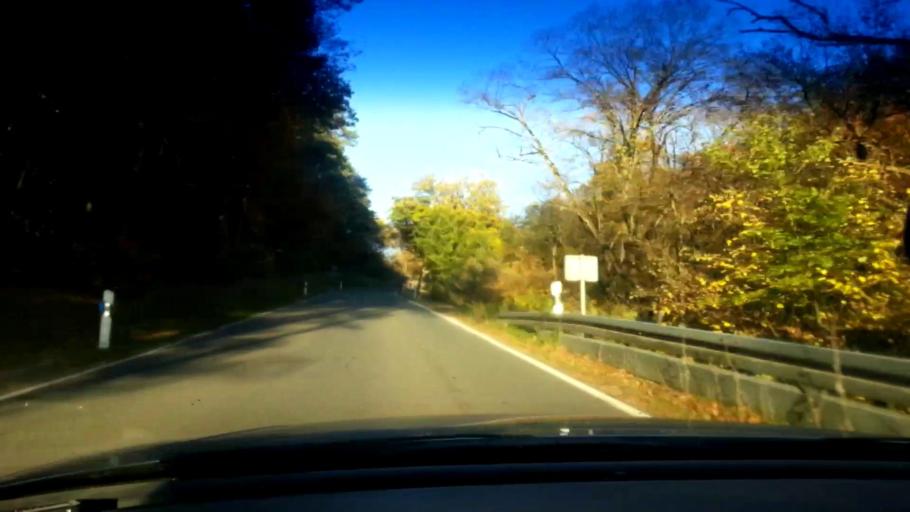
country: DE
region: Bavaria
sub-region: Upper Franconia
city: Unterleinleiter
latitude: 49.8502
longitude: 11.2018
